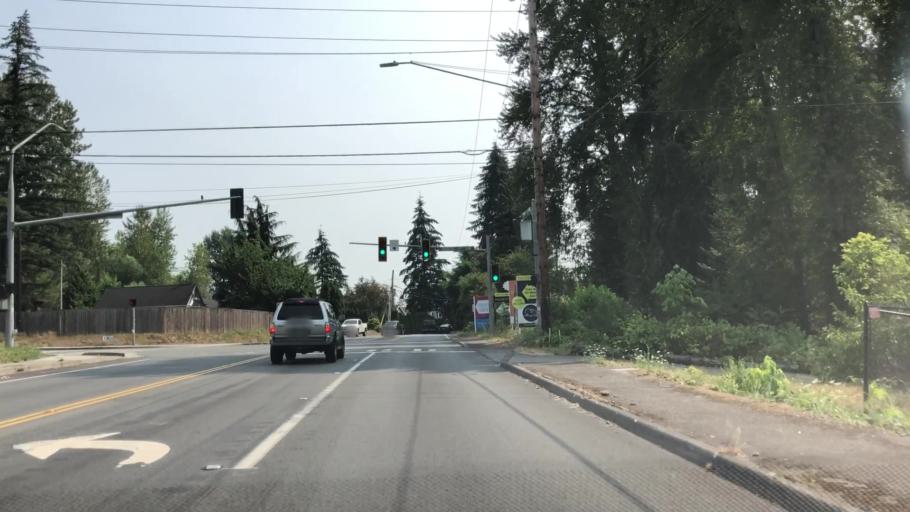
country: US
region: Washington
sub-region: Snohomish County
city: Brier
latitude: 47.7919
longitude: -122.2558
